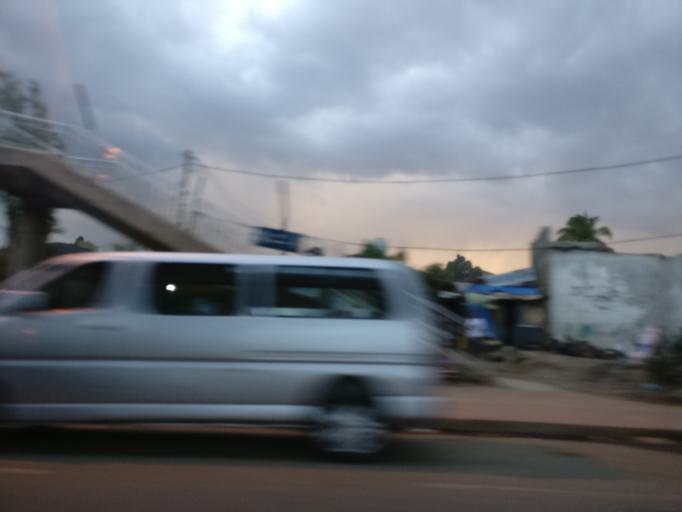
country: ET
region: Adis Abeba
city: Addis Ababa
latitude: 9.0156
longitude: 38.7346
